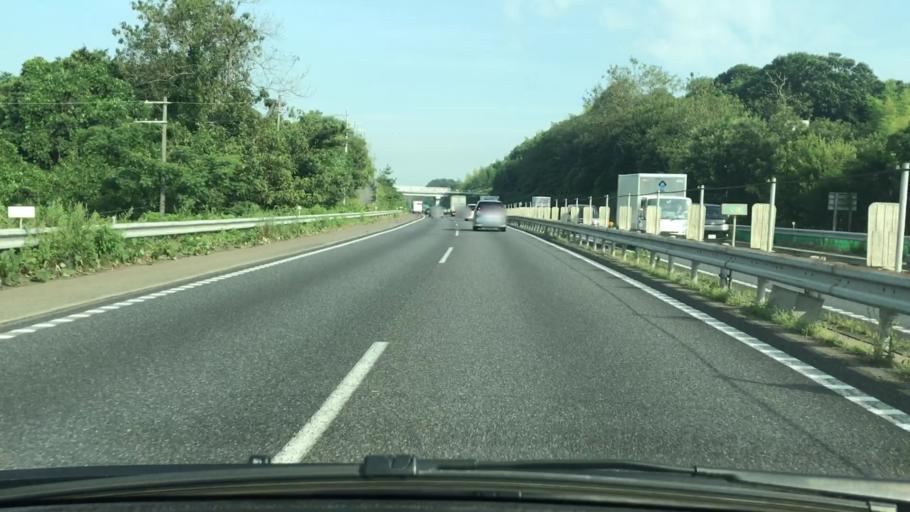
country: JP
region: Hyogo
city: Akashi
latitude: 34.6995
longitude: 134.9648
